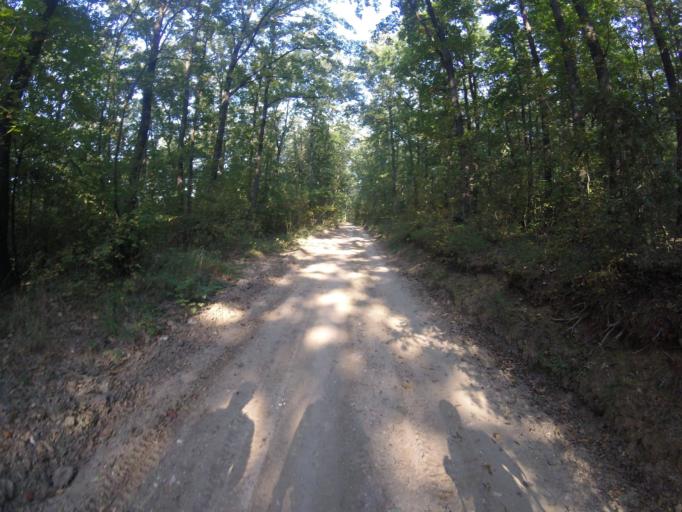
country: HU
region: Komarom-Esztergom
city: Piliscsev
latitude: 47.6900
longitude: 18.8496
